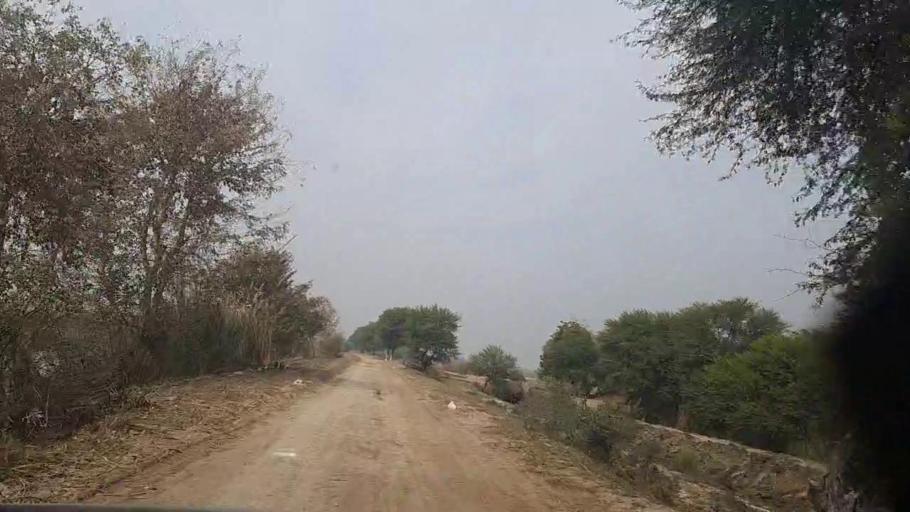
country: PK
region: Sindh
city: Daur
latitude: 26.3143
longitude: 68.2039
